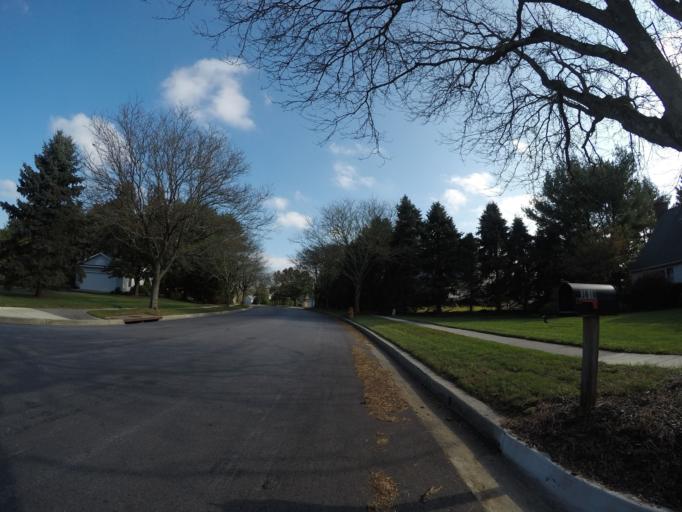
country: US
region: Maryland
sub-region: Howard County
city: Columbia
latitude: 39.2707
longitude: -76.8490
